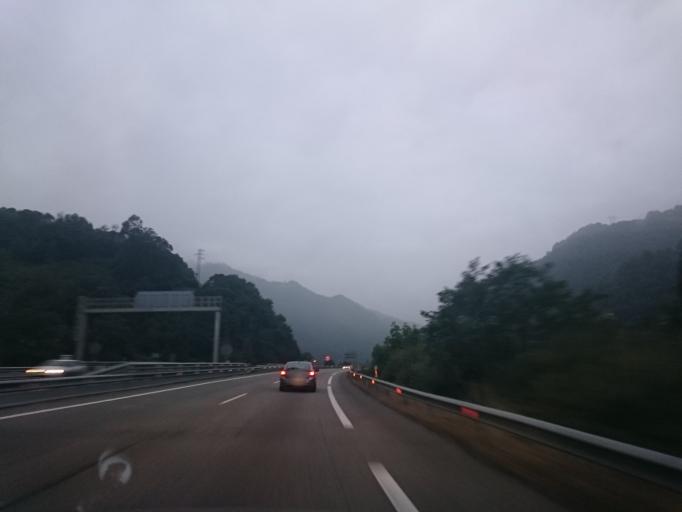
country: ES
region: Asturias
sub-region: Province of Asturias
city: Pola de Lena
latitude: 43.1972
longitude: -5.7893
